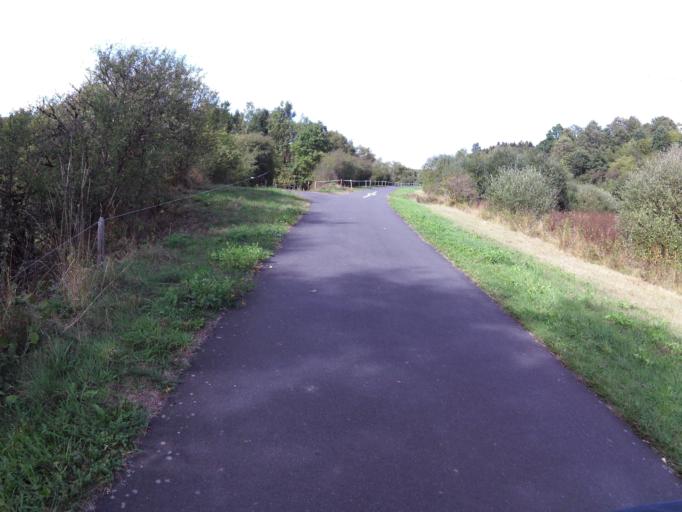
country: DE
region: Rheinland-Pfalz
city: Pronsfeld
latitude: 50.1647
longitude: 6.3179
